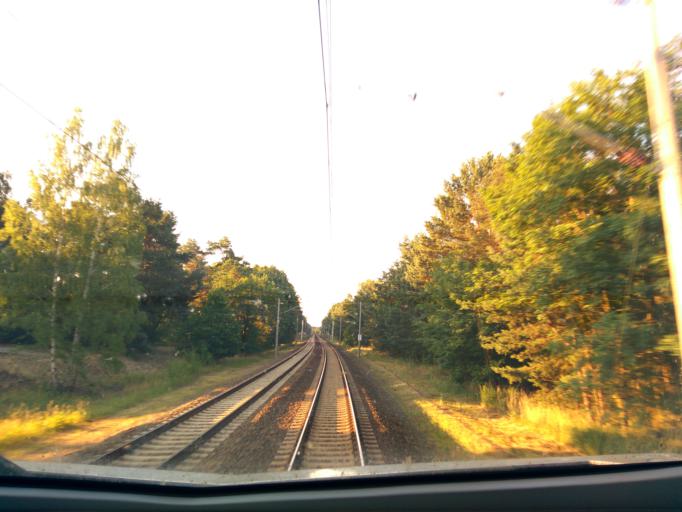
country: DE
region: Brandenburg
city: Schwerin
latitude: 52.1769
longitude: 13.6400
